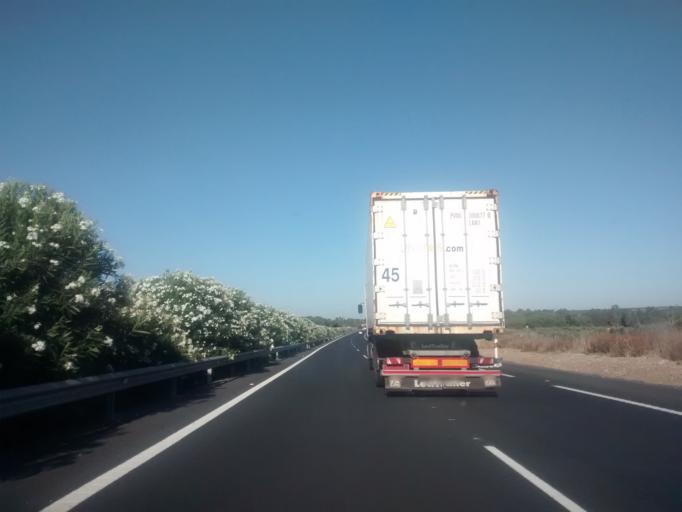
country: ES
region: Andalusia
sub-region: Provincia de Huelva
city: Bonares
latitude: 37.3407
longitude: -6.7021
